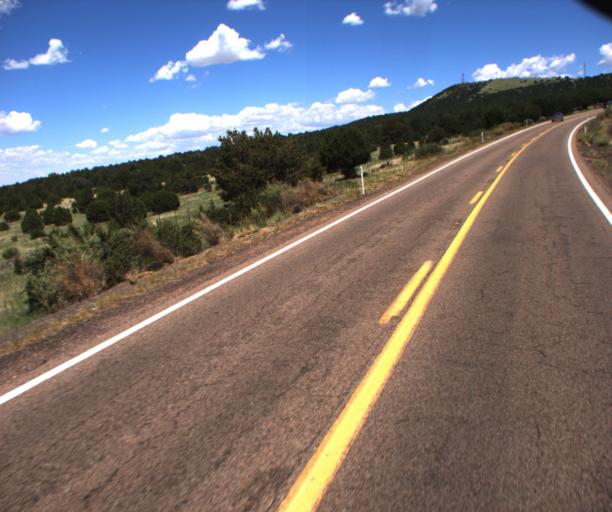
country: US
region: Arizona
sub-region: Apache County
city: Saint Johns
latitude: 34.2685
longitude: -109.5974
